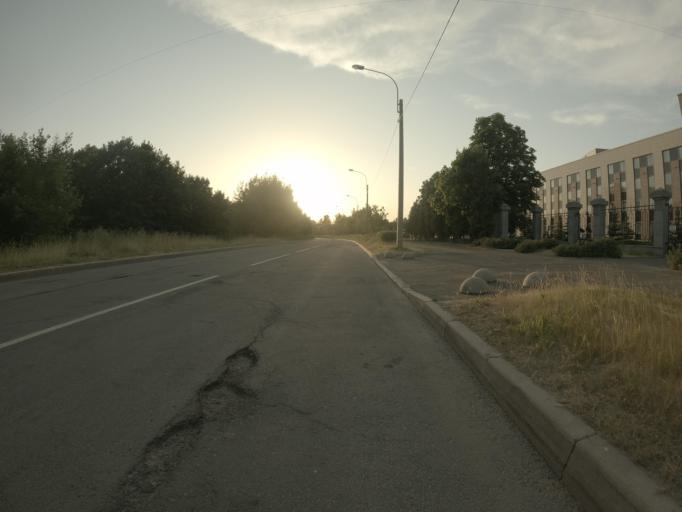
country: RU
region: St.-Petersburg
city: Krasnogvargeisky
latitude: 59.9326
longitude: 30.4283
